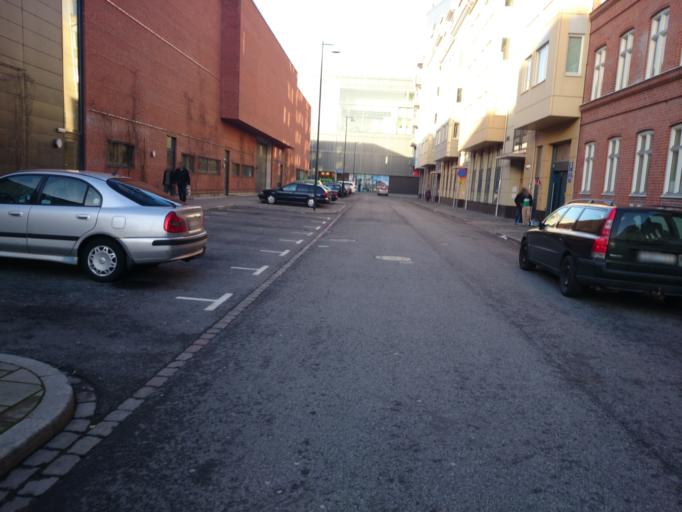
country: SE
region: Skane
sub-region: Malmo
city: Malmoe
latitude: 55.6064
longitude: 13.0241
